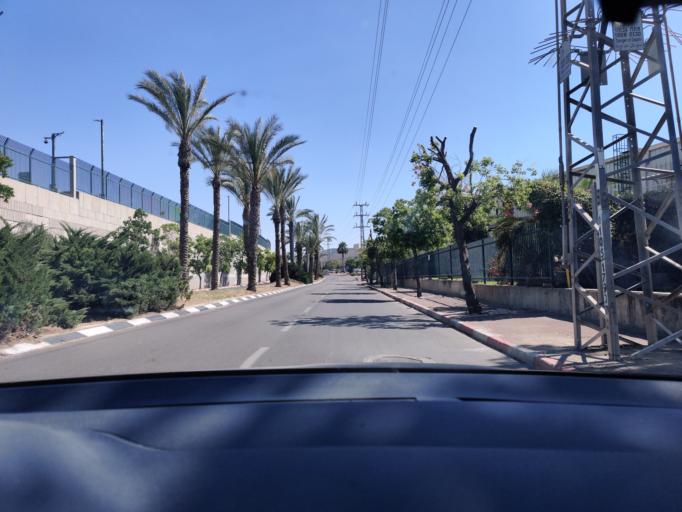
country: IL
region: Southern District
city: Qiryat Gat
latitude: 31.5988
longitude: 34.7868
